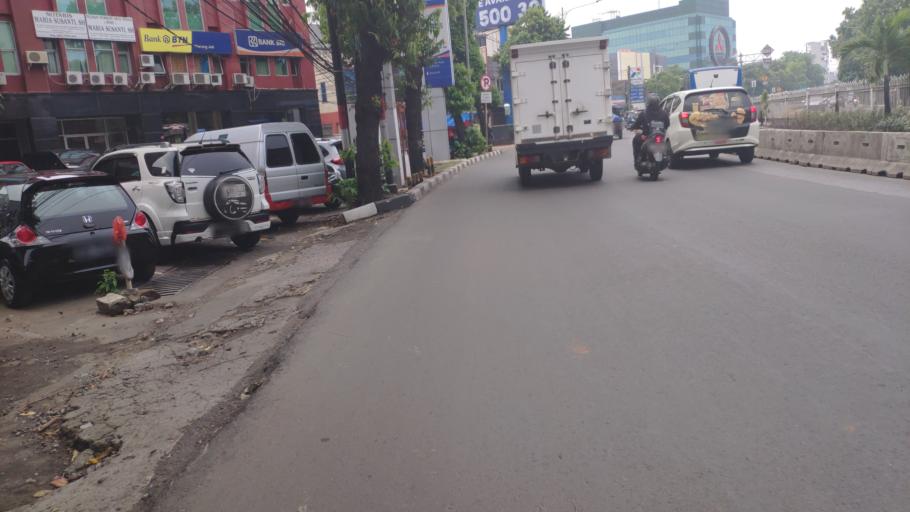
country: ID
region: Jakarta Raya
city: Jakarta
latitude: -6.2624
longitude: 106.8297
